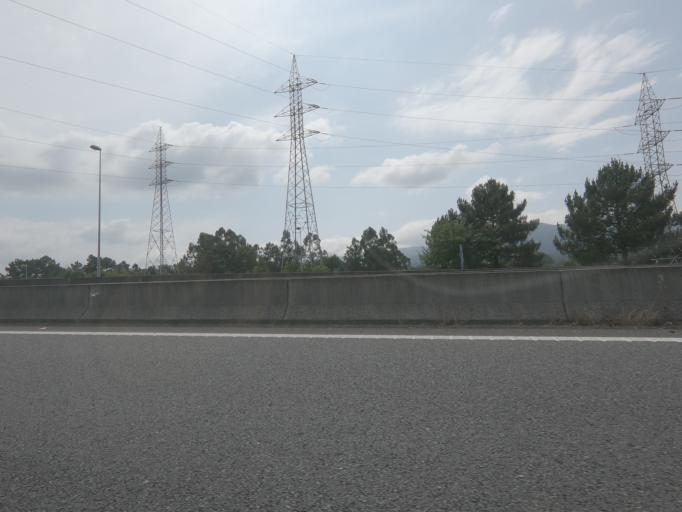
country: ES
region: Galicia
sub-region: Provincia de Pontevedra
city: Porrino
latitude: 42.1382
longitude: -8.6239
